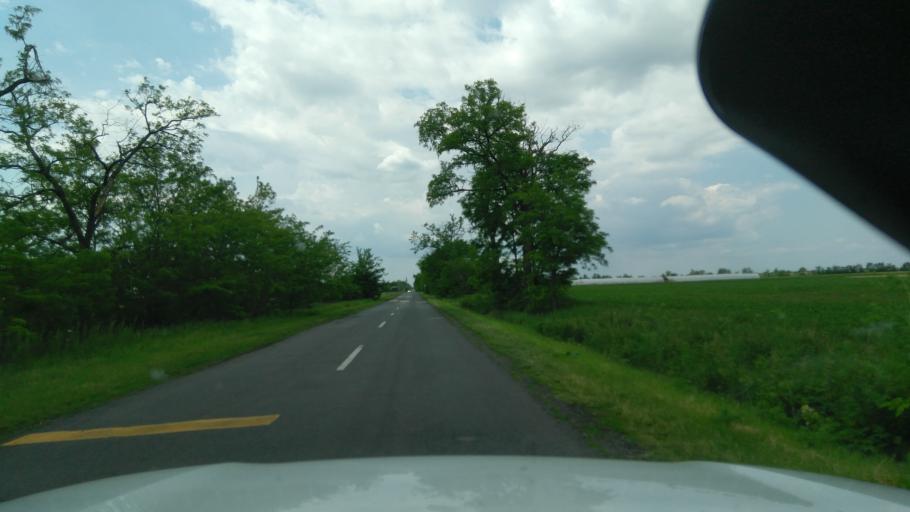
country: HU
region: Bekes
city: Magyarbanhegyes
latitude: 46.4437
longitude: 20.9845
